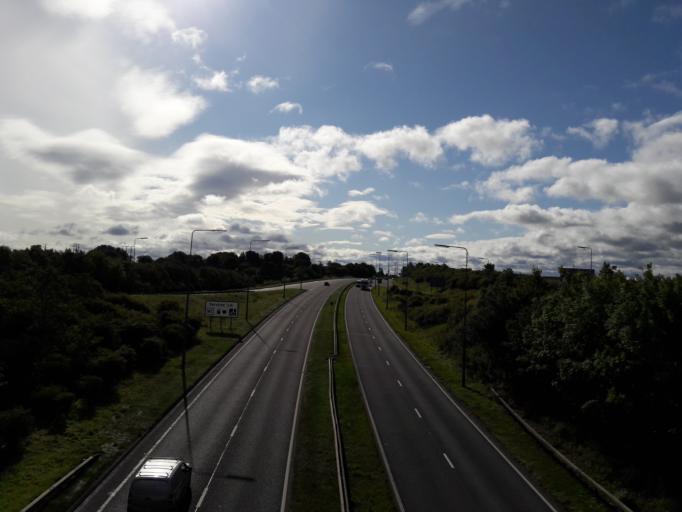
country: GB
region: England
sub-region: County Durham
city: Hawthorn
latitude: 54.8131
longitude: -1.3631
